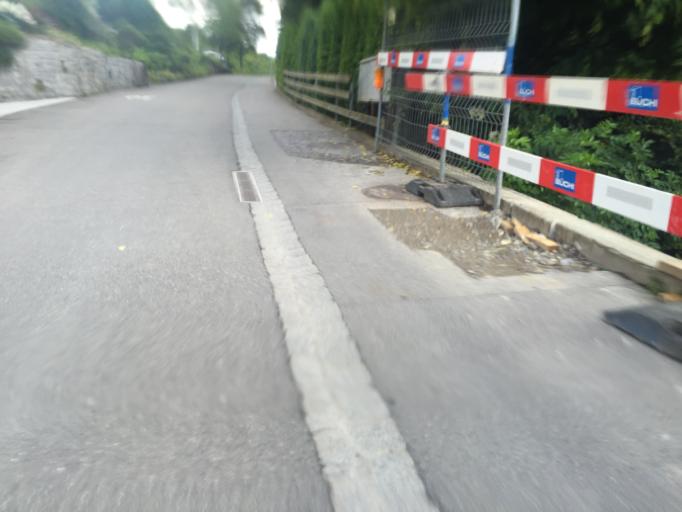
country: CH
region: Bern
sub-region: Bern-Mittelland District
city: Wohlen
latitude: 46.9682
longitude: 7.3635
